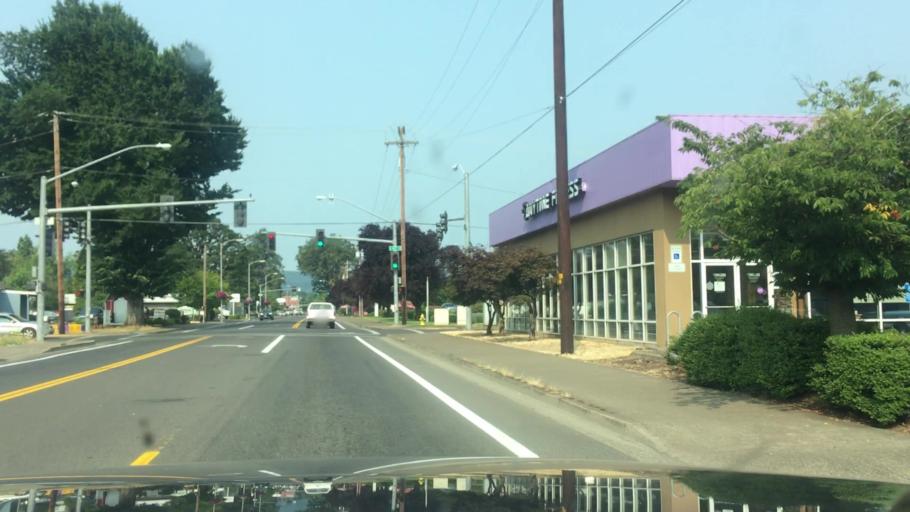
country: US
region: Oregon
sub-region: Lane County
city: Cottage Grove
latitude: 43.7972
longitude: -123.0507
